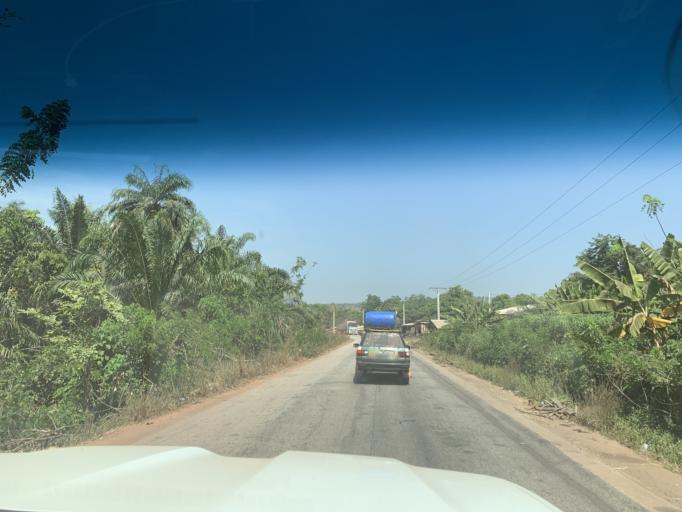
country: GN
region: Kindia
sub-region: Kindia
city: Kindia
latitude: 10.1154
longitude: -12.5468
